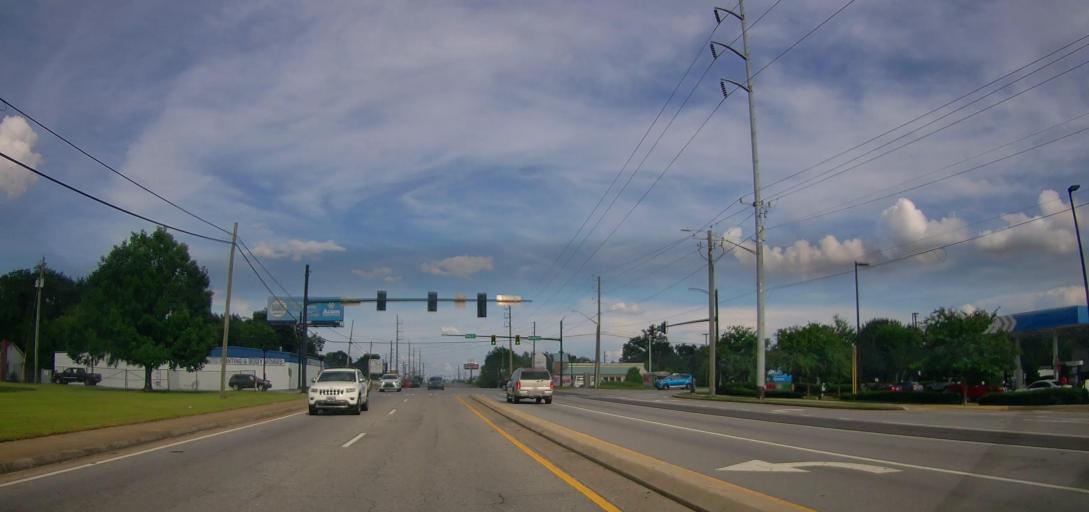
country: US
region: Alabama
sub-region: Russell County
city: Phenix City
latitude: 32.5071
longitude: -84.9767
